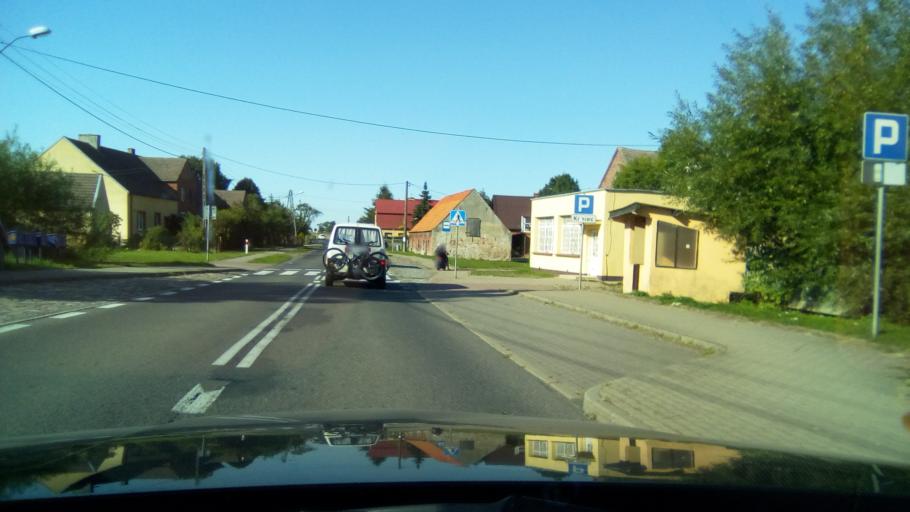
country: PL
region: West Pomeranian Voivodeship
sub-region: Powiat kamienski
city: Golczewo
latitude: 53.8274
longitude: 14.8935
